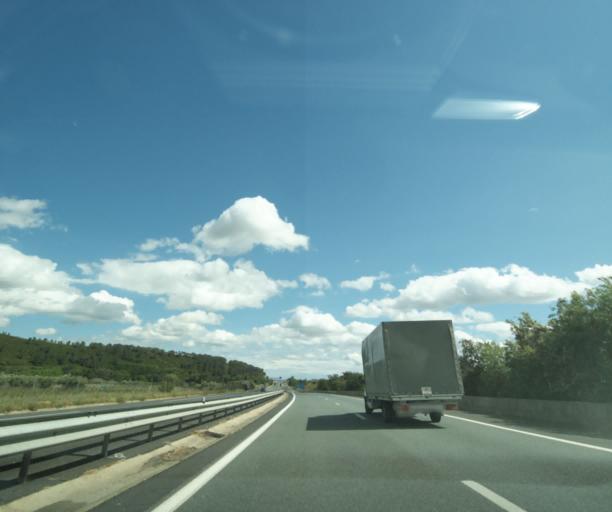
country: FR
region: Languedoc-Roussillon
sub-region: Departement de l'Herault
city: Nebian
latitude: 43.6681
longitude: 3.4299
